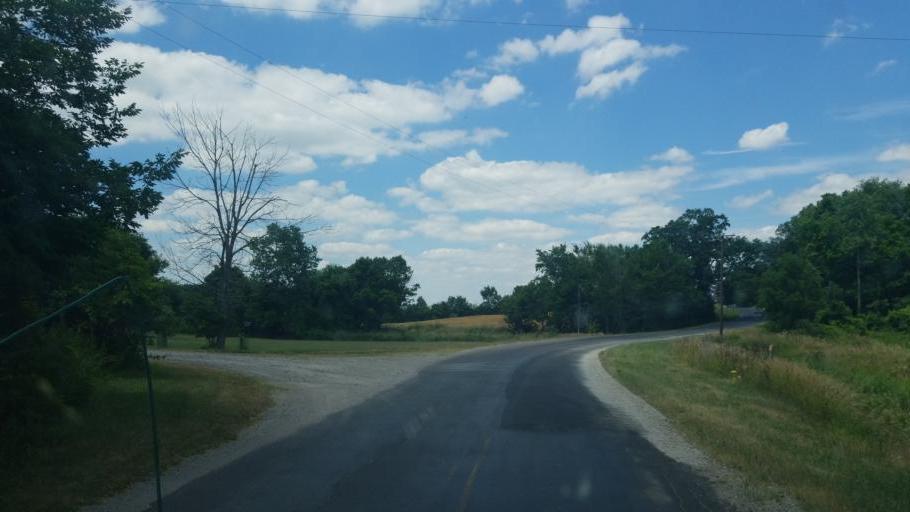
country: US
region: Ohio
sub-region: Williams County
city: Edgerton
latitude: 41.4540
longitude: -84.7106
